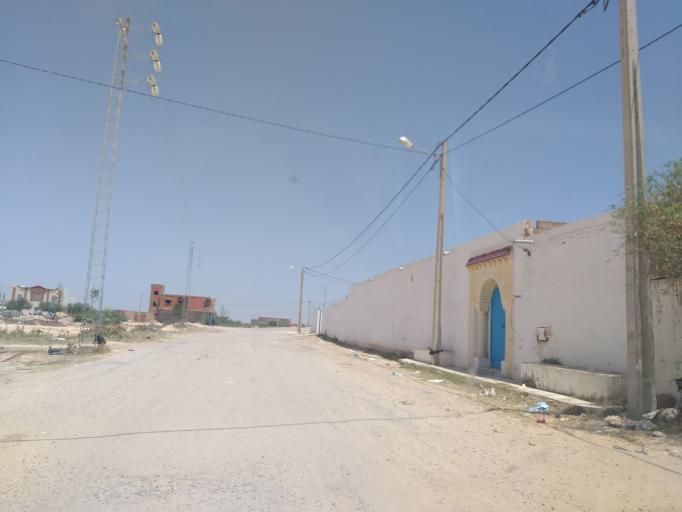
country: TN
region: Al Mahdiyah
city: El Jem
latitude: 35.3107
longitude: 10.7038
